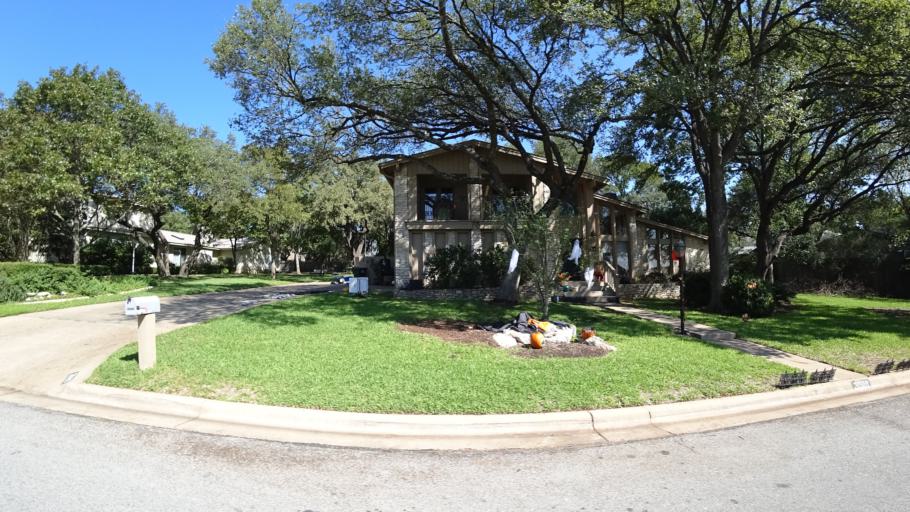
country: US
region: Texas
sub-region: Travis County
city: Rollingwood
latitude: 30.2724
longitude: -97.8094
